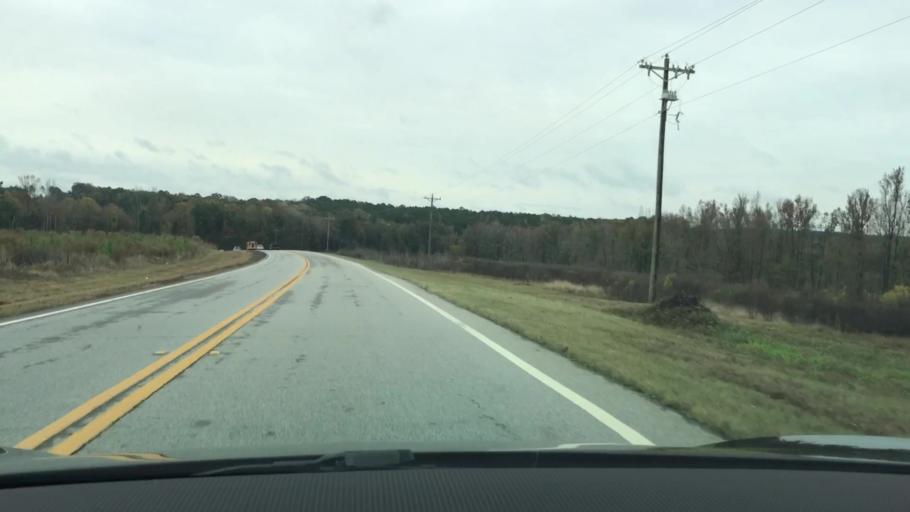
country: US
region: Georgia
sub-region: Greene County
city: Greensboro
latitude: 33.6141
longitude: -83.2093
